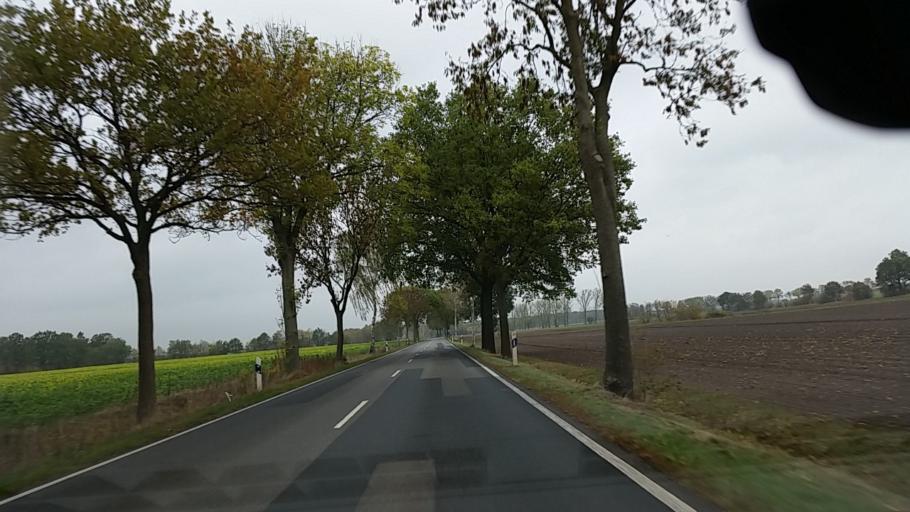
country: DE
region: Lower Saxony
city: Tulau
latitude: 52.6446
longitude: 10.8087
